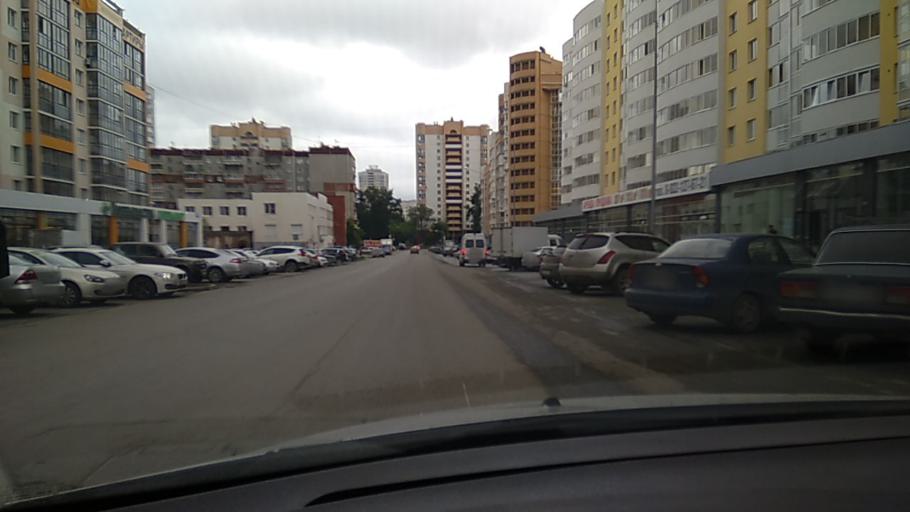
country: RU
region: Sverdlovsk
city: Yekaterinburg
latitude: 56.8054
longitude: 60.6142
